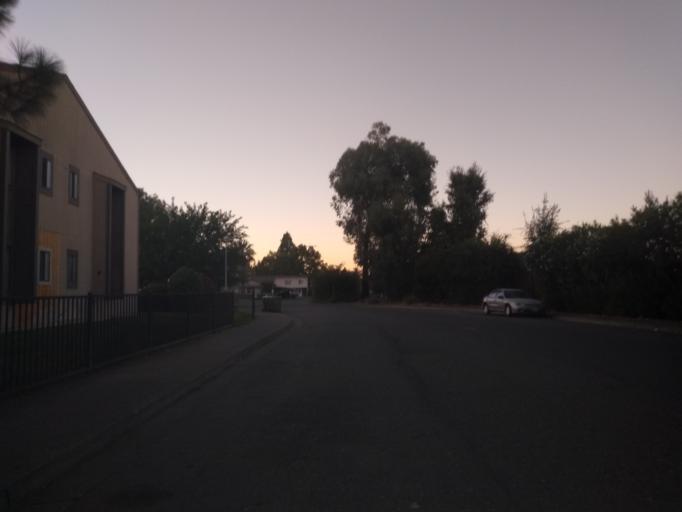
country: US
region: California
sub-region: Mendocino County
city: Ukiah
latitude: 39.1368
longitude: -123.2065
